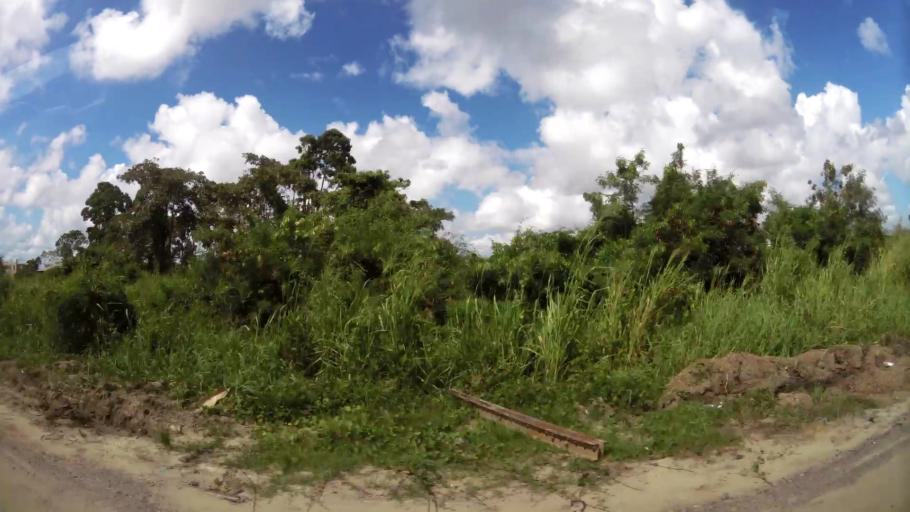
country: SR
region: Paramaribo
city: Paramaribo
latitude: 5.8646
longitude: -55.1292
